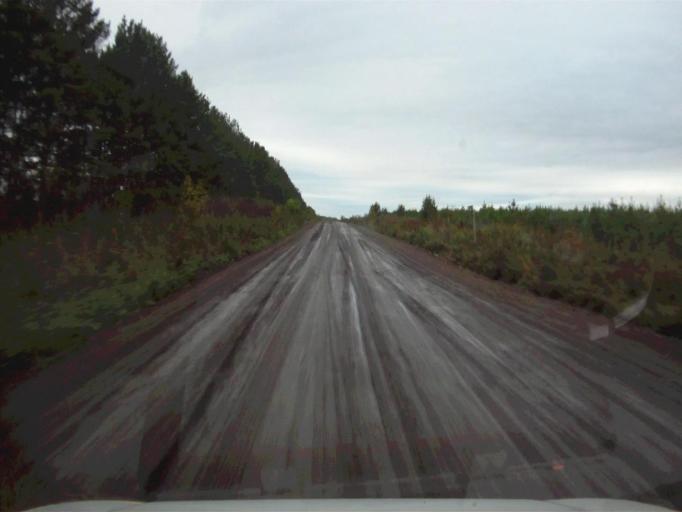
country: RU
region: Chelyabinsk
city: Nyazepetrovsk
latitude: 56.1443
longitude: 59.2848
